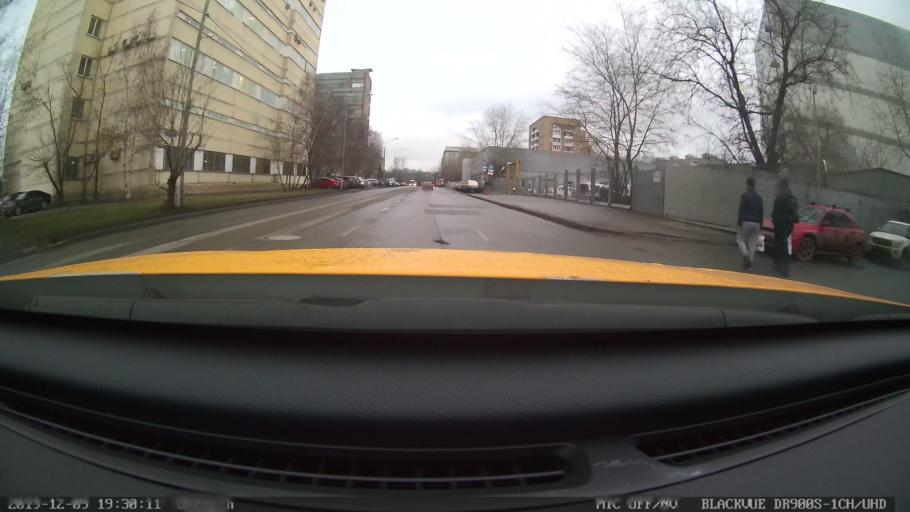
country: RU
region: Moscow
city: Ryazanskiy
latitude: 55.7556
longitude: 37.7587
